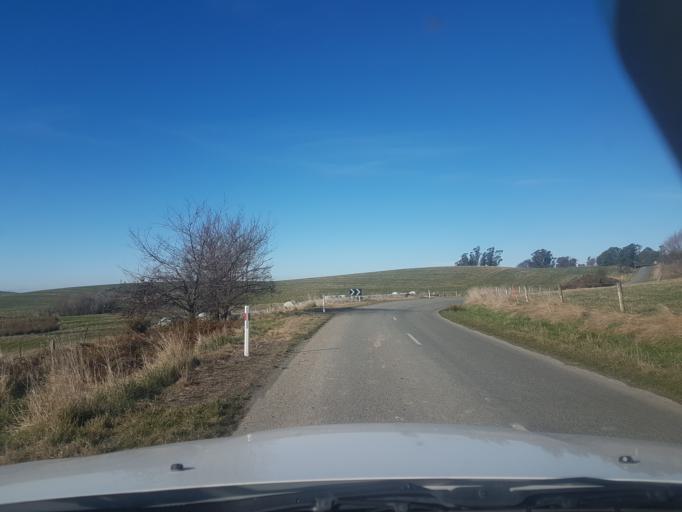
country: NZ
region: Canterbury
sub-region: Timaru District
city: Pleasant Point
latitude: -44.3778
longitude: 171.0880
